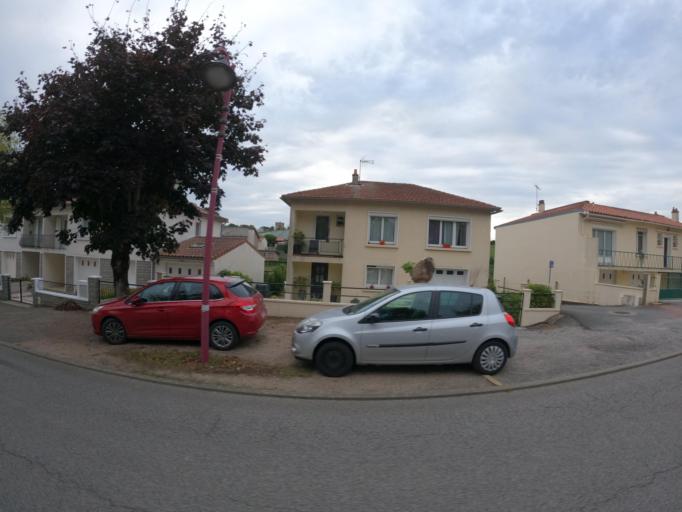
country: FR
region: Poitou-Charentes
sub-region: Departement des Deux-Sevres
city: Parthenay
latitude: 46.6576
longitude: -0.2485
